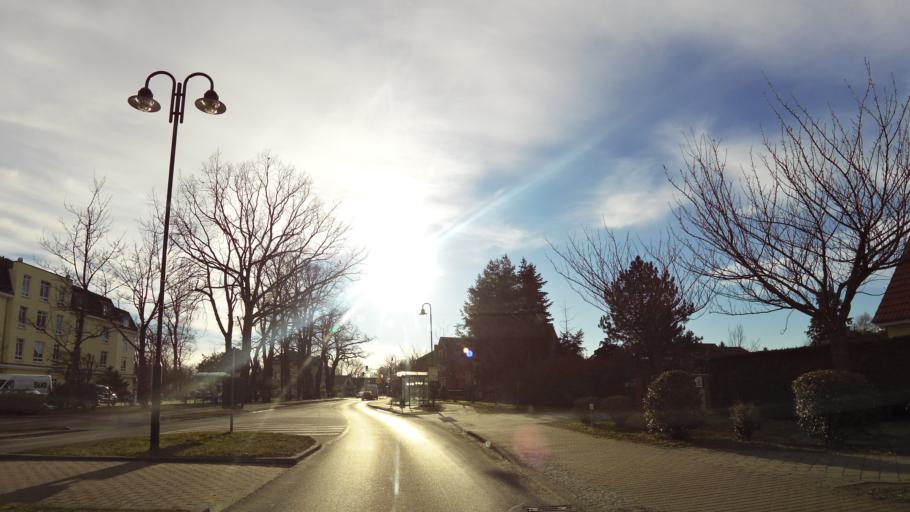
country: DE
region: Brandenburg
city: Petershagen
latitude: 52.5161
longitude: 13.7485
